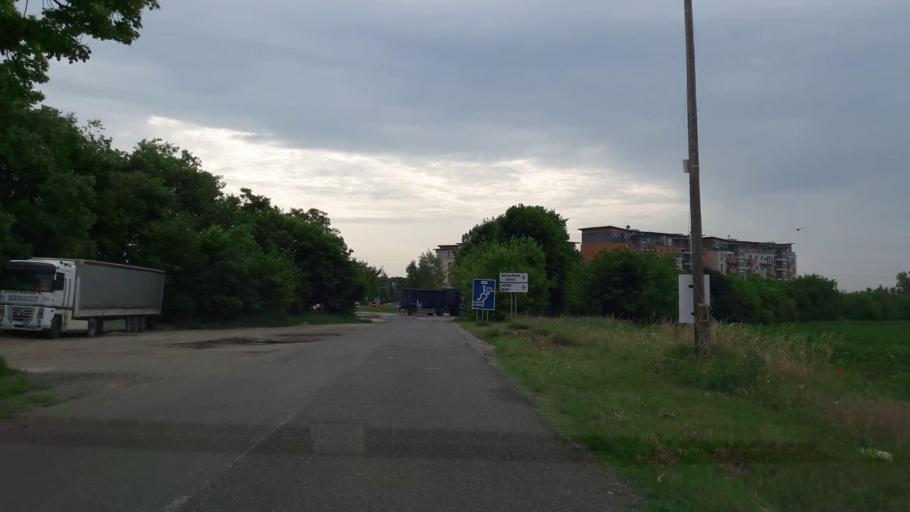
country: SK
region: Bratislavsky
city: Senec
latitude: 48.2229
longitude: 17.3836
